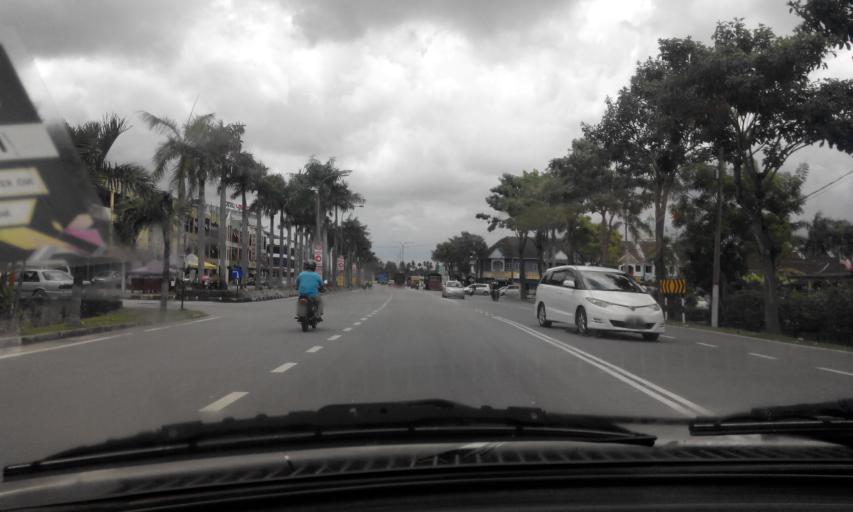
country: MY
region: Perak
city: Parit Buntar
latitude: 5.1143
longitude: 100.4868
